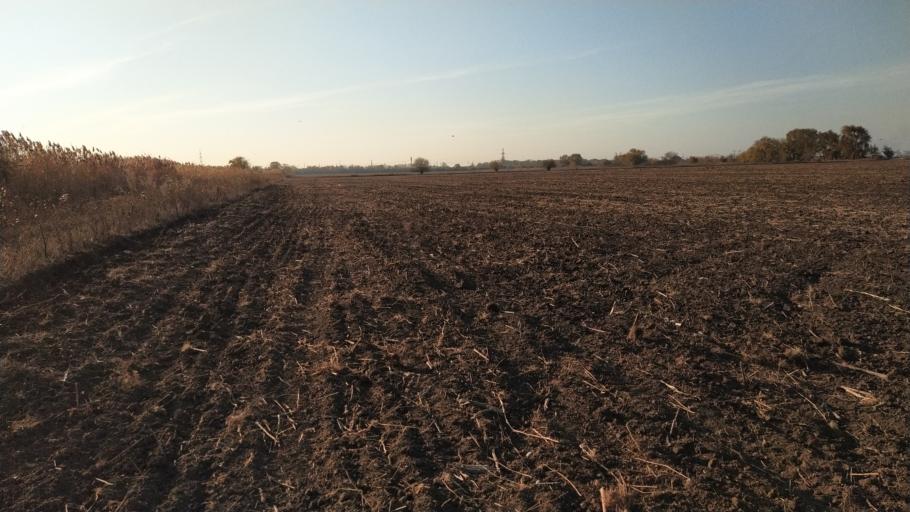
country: RU
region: Rostov
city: Bataysk
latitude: 47.1215
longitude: 39.7258
